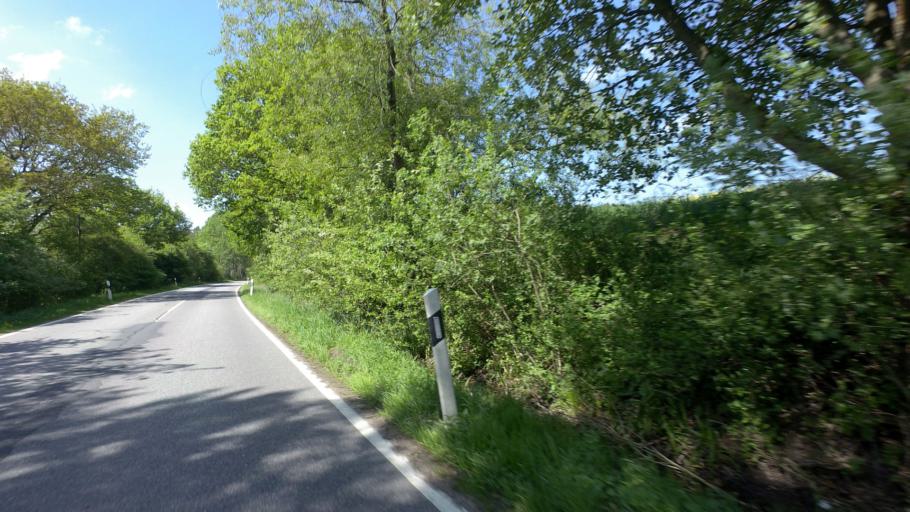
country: DE
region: Mecklenburg-Vorpommern
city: Mollenhagen
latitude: 53.5703
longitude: 12.8987
